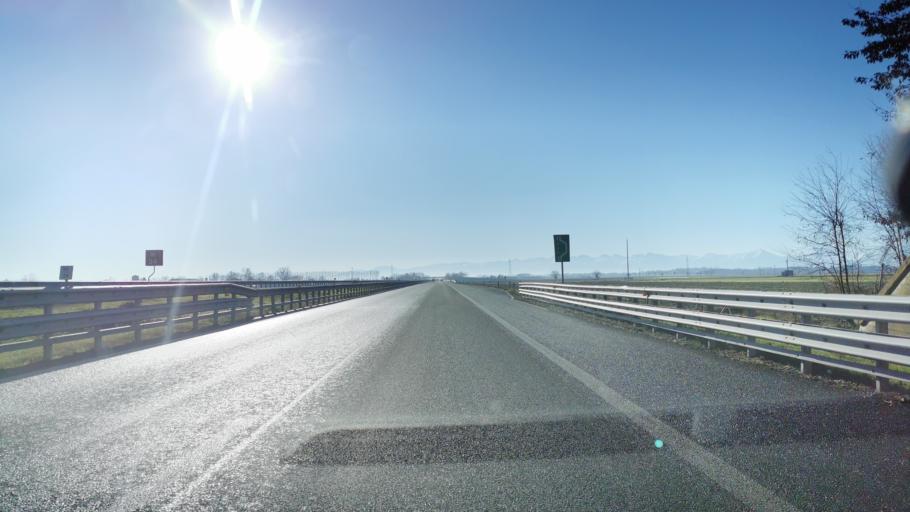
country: IT
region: Piedmont
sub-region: Provincia di Cuneo
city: Sommariva del Bosco
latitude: 44.7353
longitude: 7.7540
